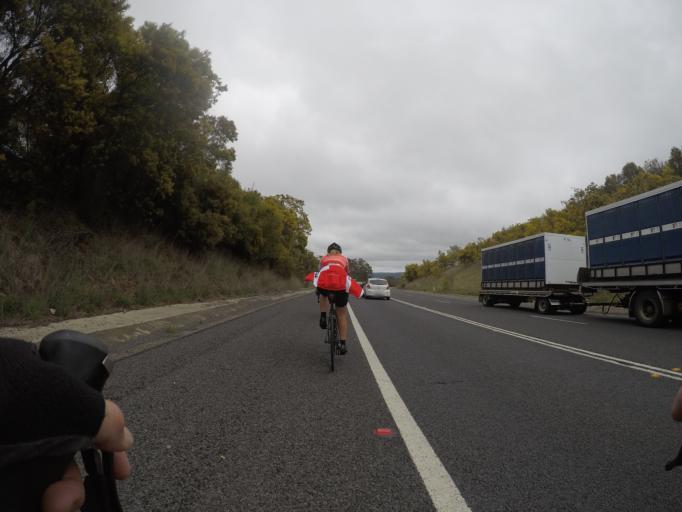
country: AU
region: New South Wales
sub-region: Lithgow
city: Portland
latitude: -33.4504
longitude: 149.9604
